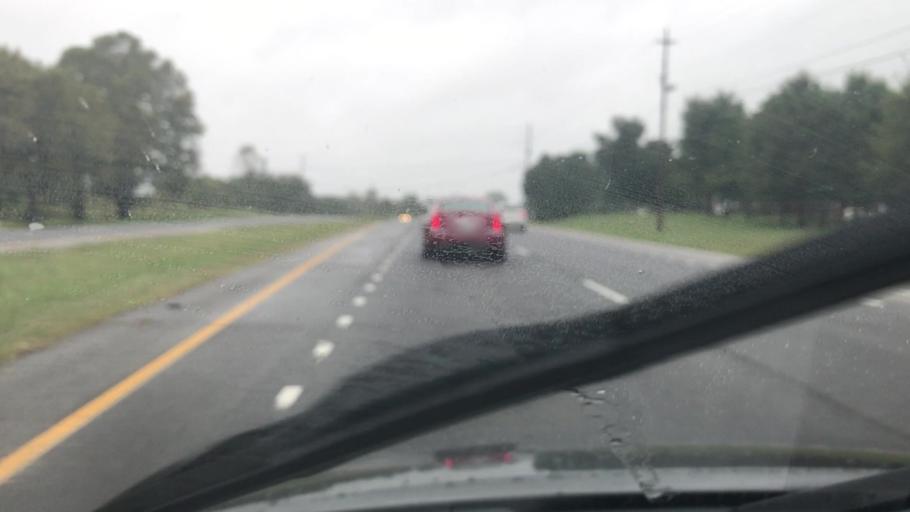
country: US
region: Tennessee
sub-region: Cheatham County
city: Ashland City
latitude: 36.2209
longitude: -87.0002
